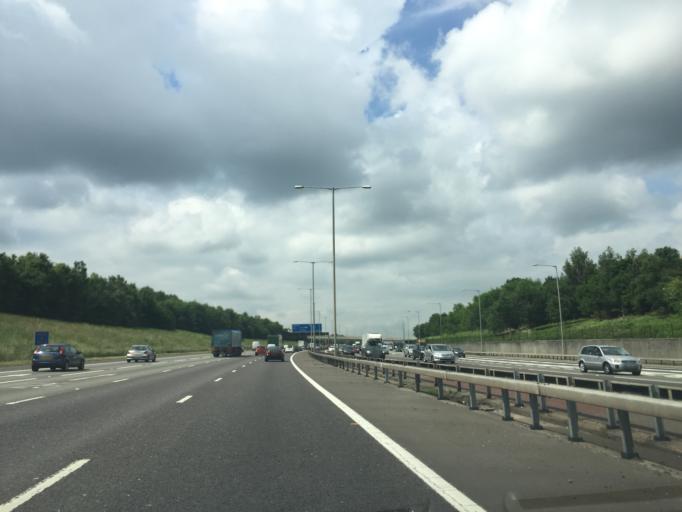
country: GB
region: England
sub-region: Buckinghamshire
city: Denham
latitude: 51.5493
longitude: -0.5211
